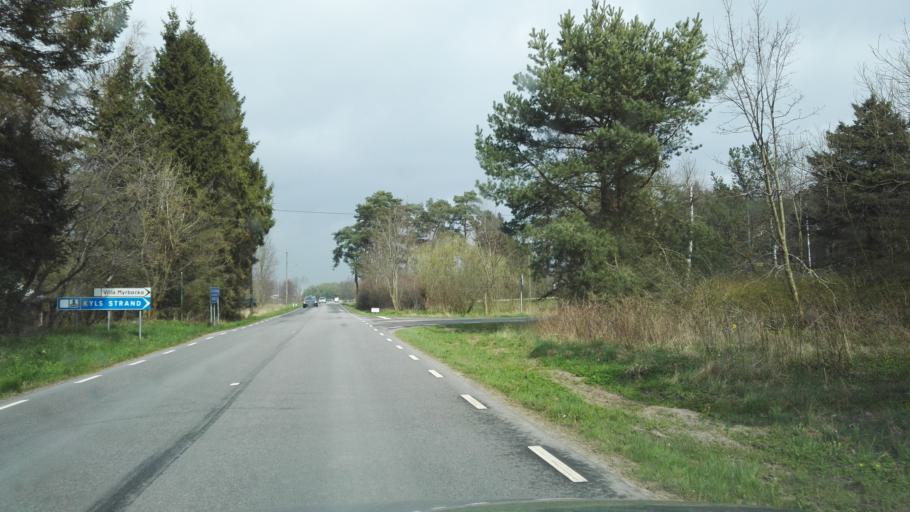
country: SE
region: Skane
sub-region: Simrishamns Kommun
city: Simrishamn
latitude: 55.4388
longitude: 14.2343
